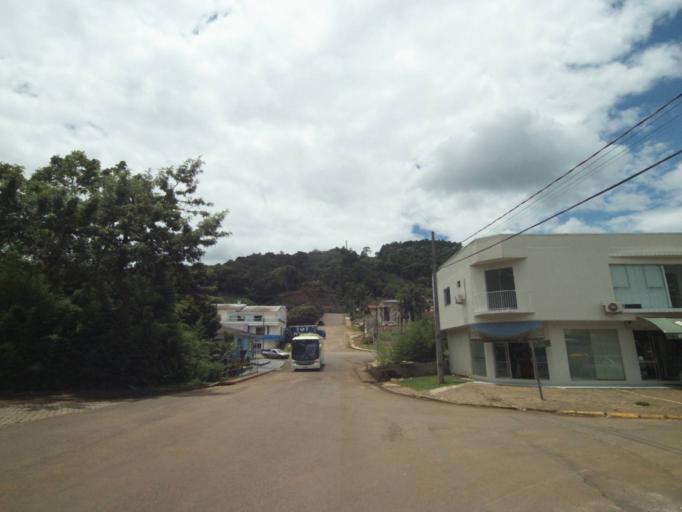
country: BR
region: Parana
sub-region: Uniao Da Vitoria
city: Uniao da Vitoria
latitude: -26.1586
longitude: -51.5537
